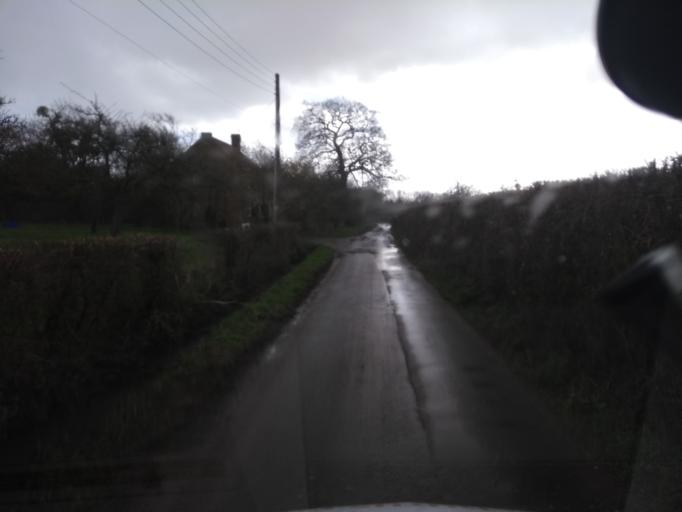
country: GB
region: England
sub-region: Somerset
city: South Petherton
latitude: 50.9770
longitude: -2.8177
